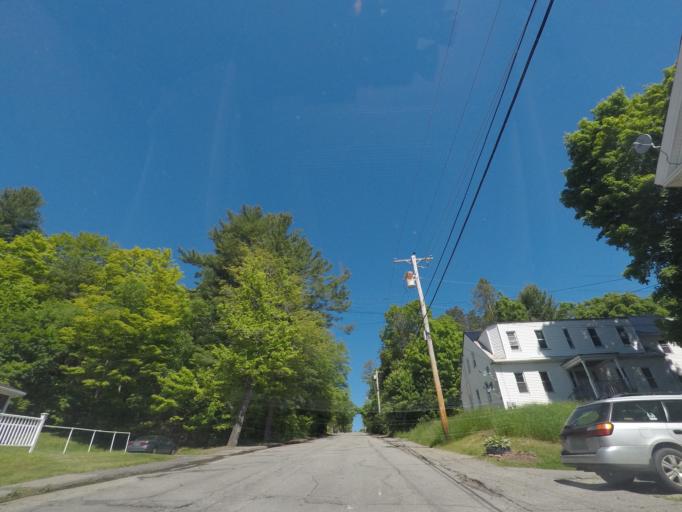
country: US
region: Maine
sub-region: Kennebec County
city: Gardiner
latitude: 44.2303
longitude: -69.7780
